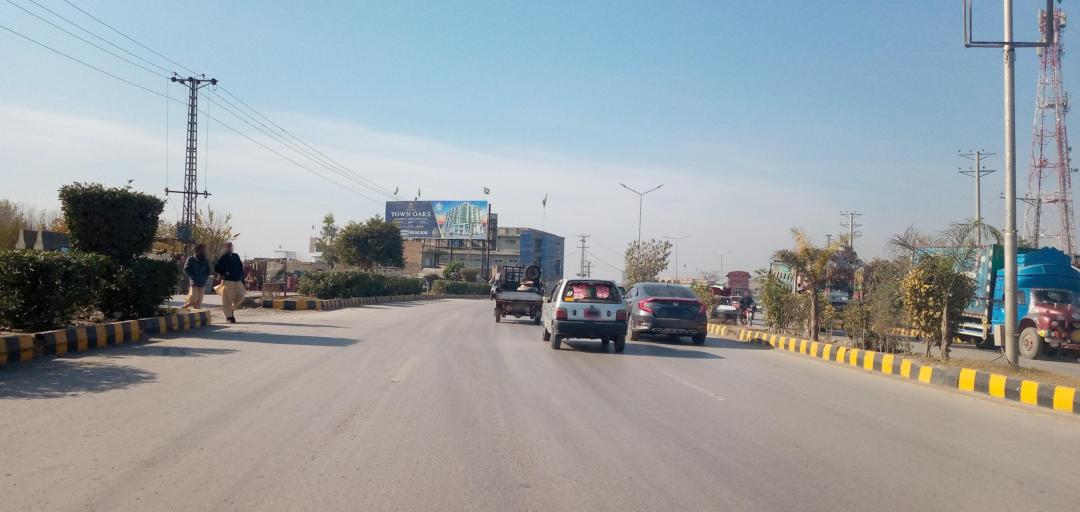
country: PK
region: Khyber Pakhtunkhwa
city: Peshawar
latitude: 33.9597
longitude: 71.5092
